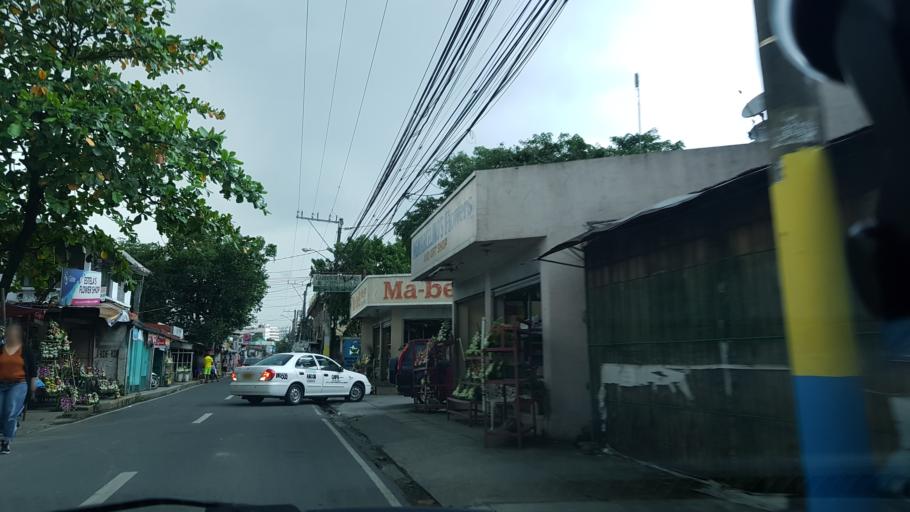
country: PH
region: Calabarzon
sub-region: Province of Rizal
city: Pateros
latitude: 14.5379
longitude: 121.0687
